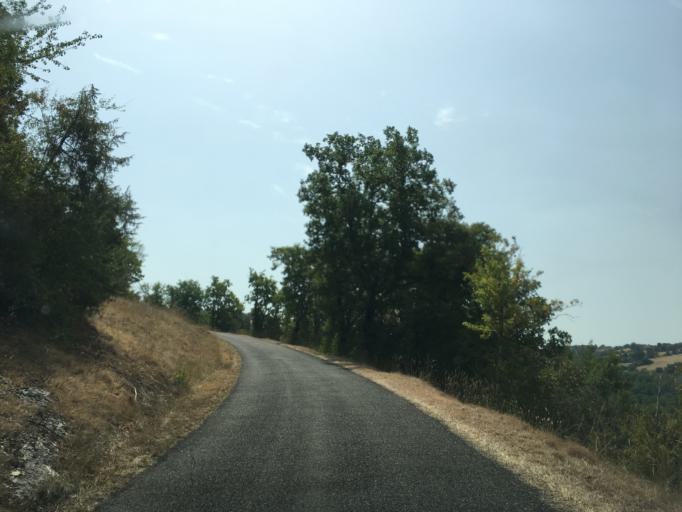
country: FR
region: Midi-Pyrenees
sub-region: Departement du Lot
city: Le Vigan
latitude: 44.7599
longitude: 1.5510
